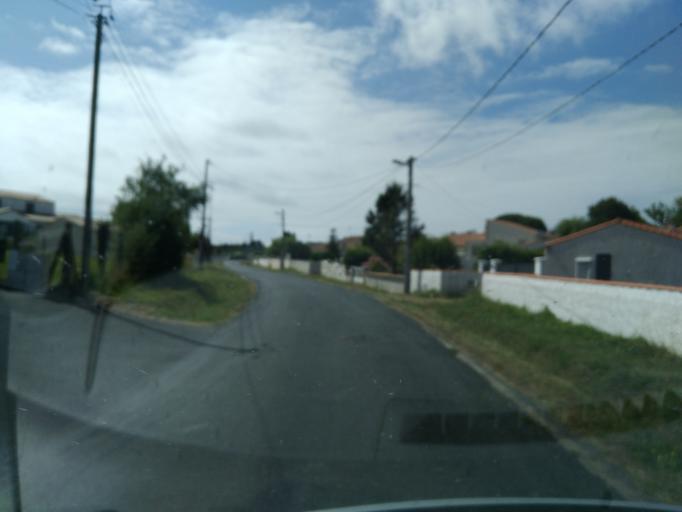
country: FR
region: Poitou-Charentes
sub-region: Departement de la Charente-Maritime
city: Saint-Palais-sur-Mer
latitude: 45.6751
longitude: -1.0875
